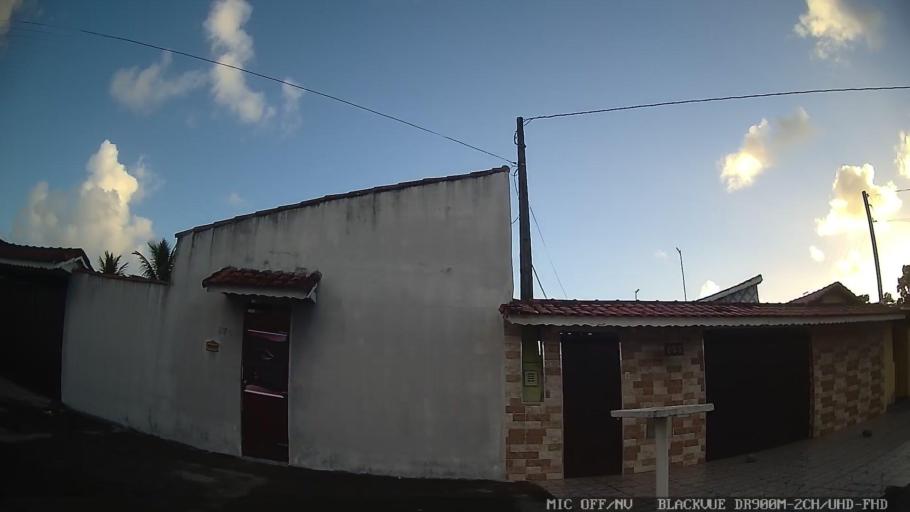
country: BR
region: Sao Paulo
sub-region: Itanhaem
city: Itanhaem
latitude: -24.1455
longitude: -46.7258
